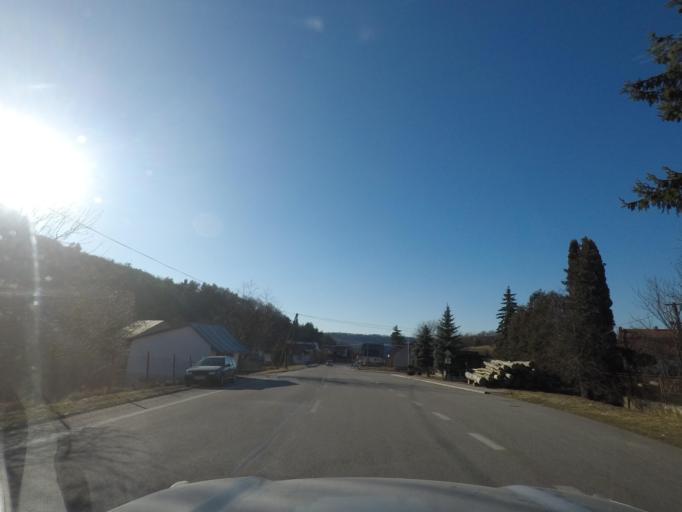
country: SK
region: Presovsky
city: Medzilaborce
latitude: 49.2470
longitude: 21.9309
